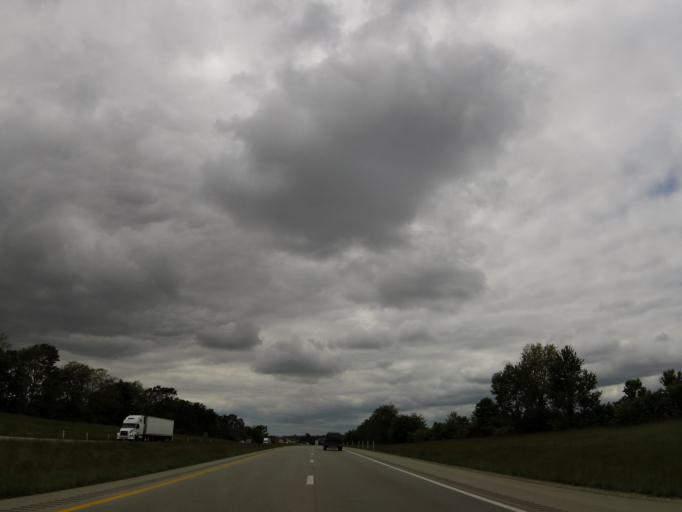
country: US
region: Kentucky
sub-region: Scott County
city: Georgetown
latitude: 38.1503
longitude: -84.5914
